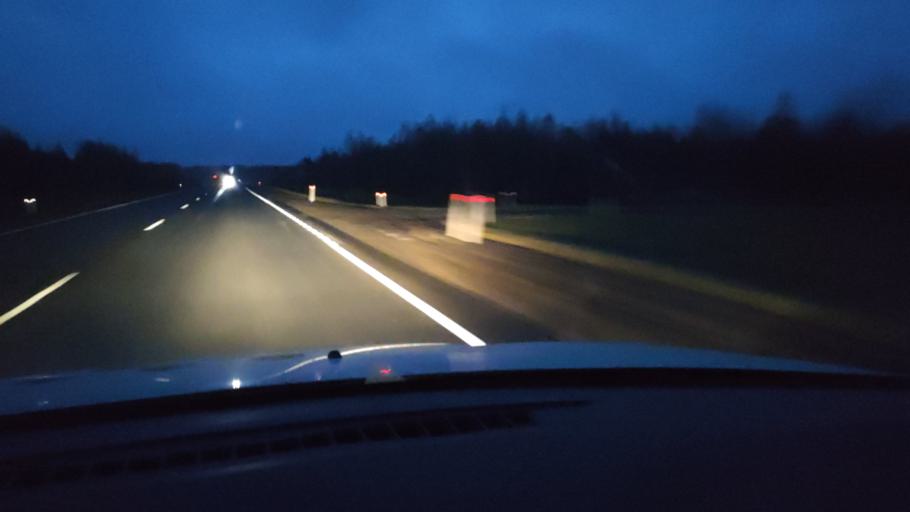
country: RU
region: Kirov
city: Kostino
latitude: 58.7090
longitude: 53.7002
